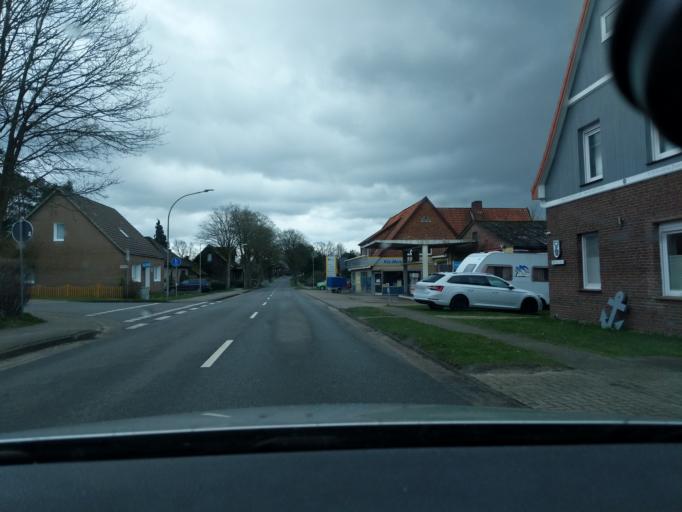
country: DE
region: Lower Saxony
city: Kutenholz
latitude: 53.5078
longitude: 9.3021
